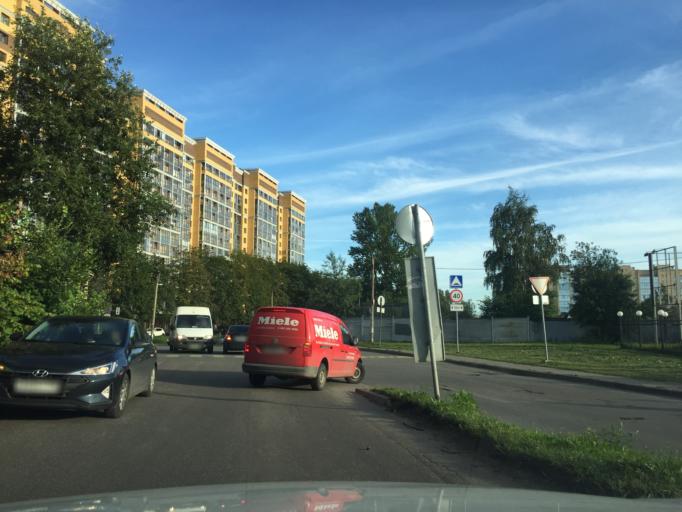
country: RU
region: St.-Petersburg
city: Admiralteisky
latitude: 59.8807
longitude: 30.3126
